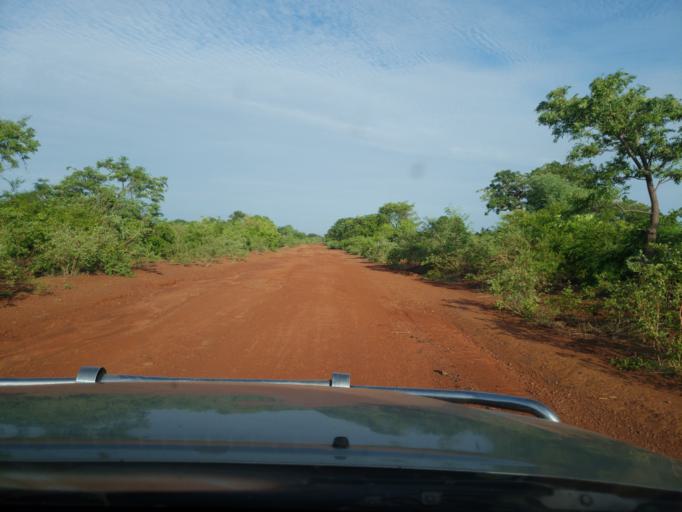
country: ML
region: Sikasso
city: Koutiala
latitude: 12.4254
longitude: -5.6508
